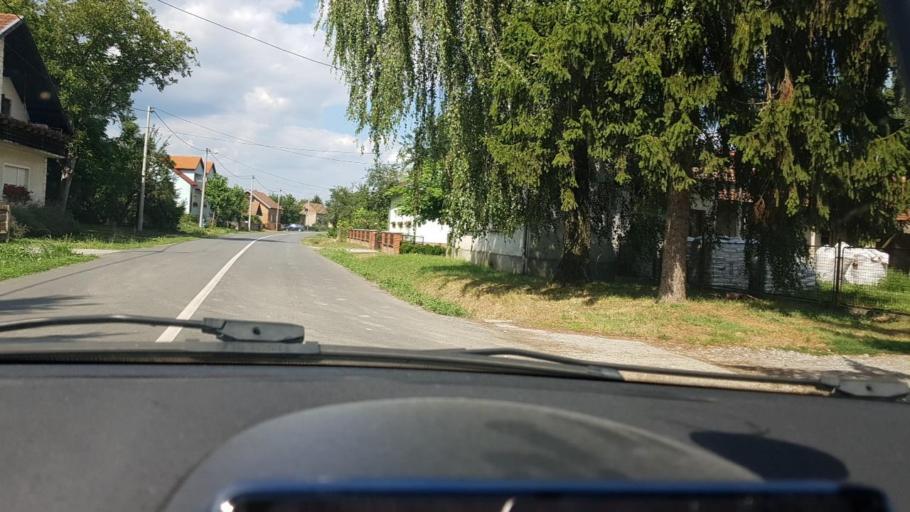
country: HR
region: Bjelovarsko-Bilogorska
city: Zdralovi
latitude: 45.8505
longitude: 16.9767
